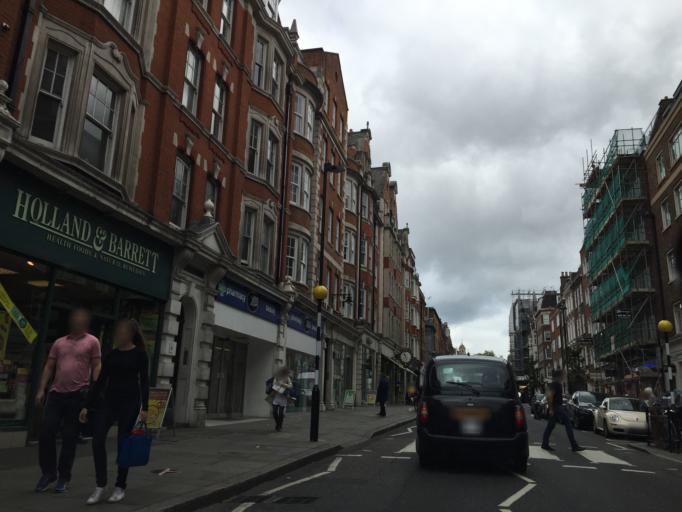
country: GB
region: England
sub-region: Greater London
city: Camden Town
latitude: 51.5191
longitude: -0.1517
